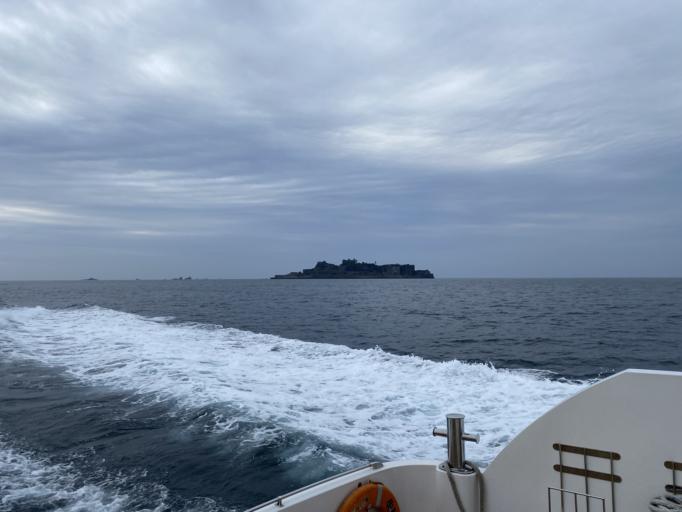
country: JP
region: Nagasaki
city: Nagasaki-shi
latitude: 32.6275
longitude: 129.7528
